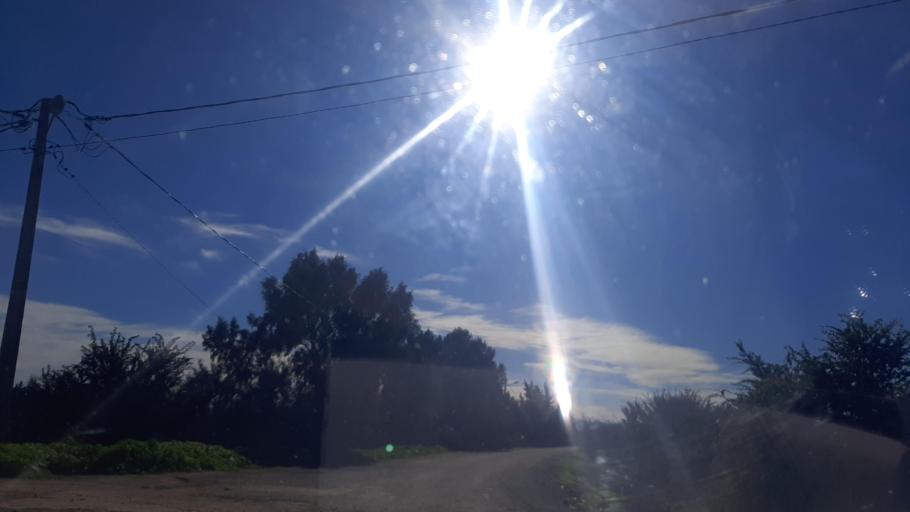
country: TN
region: Tunis
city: Oued Lill
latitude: 36.7584
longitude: 9.9817
